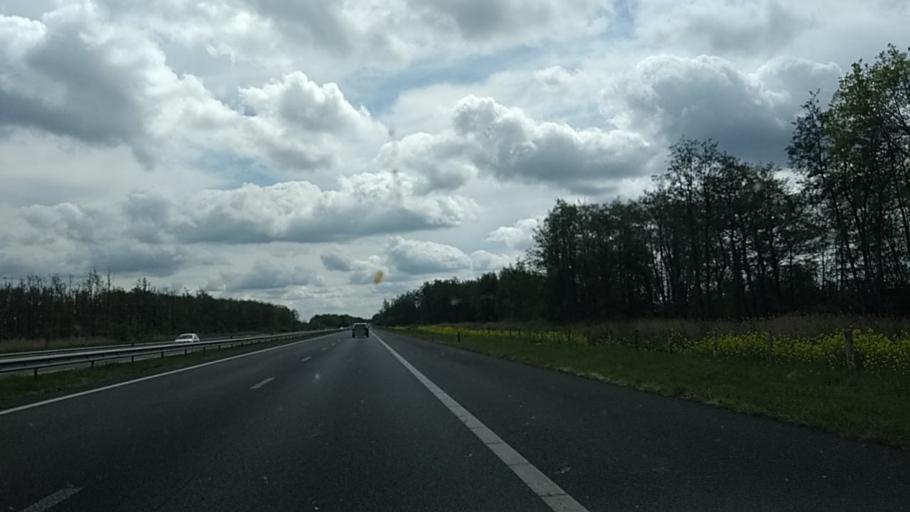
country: NL
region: Friesland
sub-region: Gemeente Weststellingwerf
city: Steggerda
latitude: 52.8562
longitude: 6.0346
